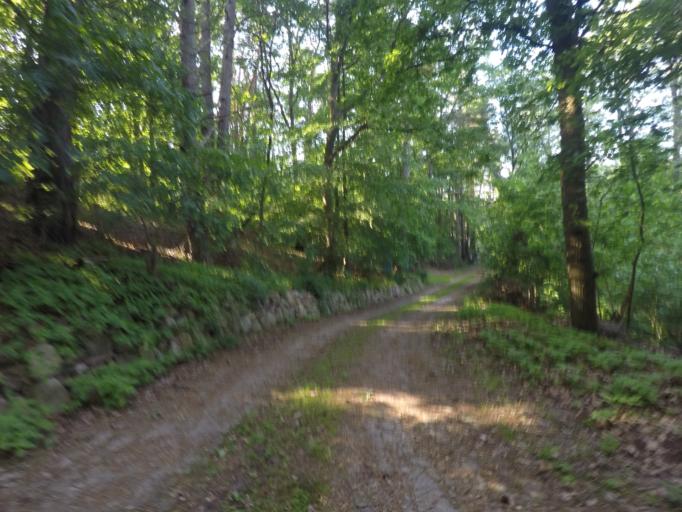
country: DE
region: Brandenburg
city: Marienwerder
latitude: 52.8715
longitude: 13.6841
